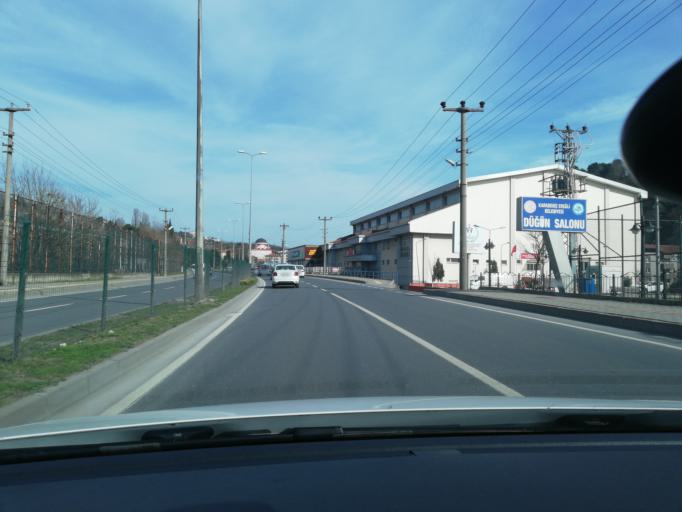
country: TR
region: Zonguldak
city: Eregli
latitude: 41.2692
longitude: 31.4411
